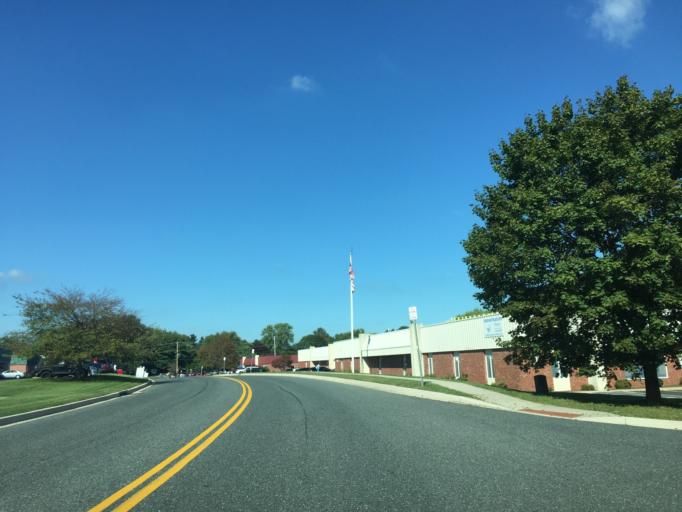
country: US
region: Maryland
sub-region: Harford County
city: Bel Air North
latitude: 39.5772
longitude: -76.3686
